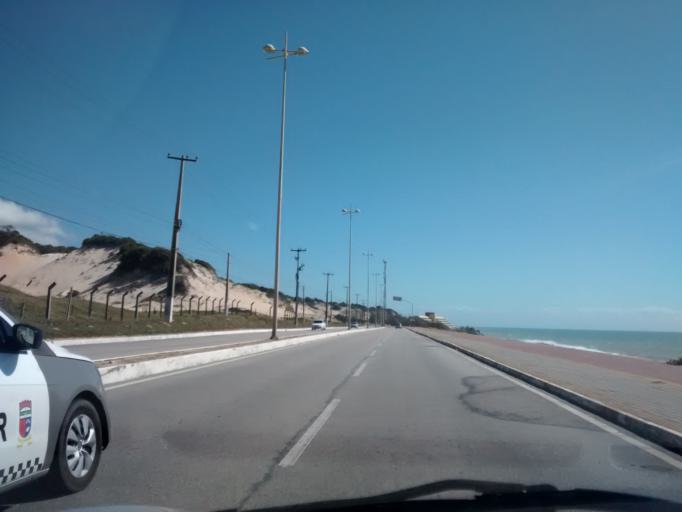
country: BR
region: Rio Grande do Norte
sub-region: Natal
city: Natal
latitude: -5.8499
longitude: -35.1822
